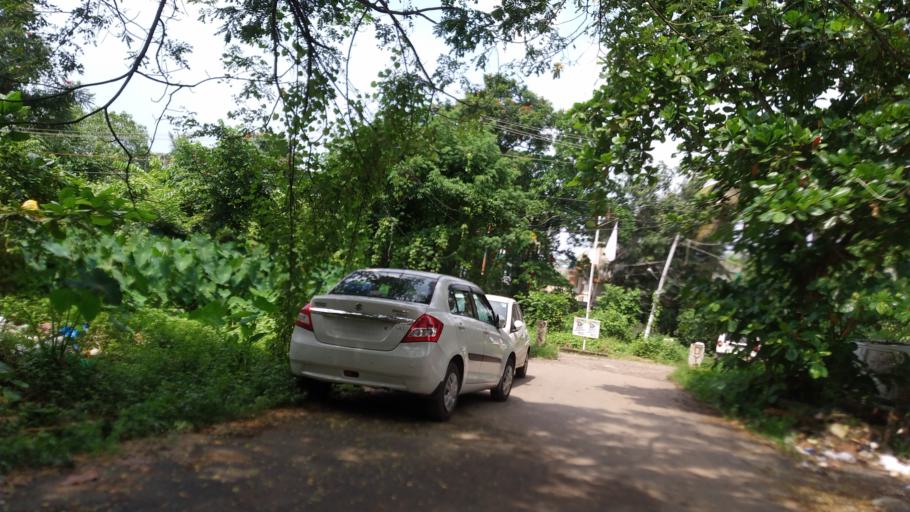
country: IN
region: Kerala
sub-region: Ernakulam
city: Cochin
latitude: 9.9695
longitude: 76.3022
